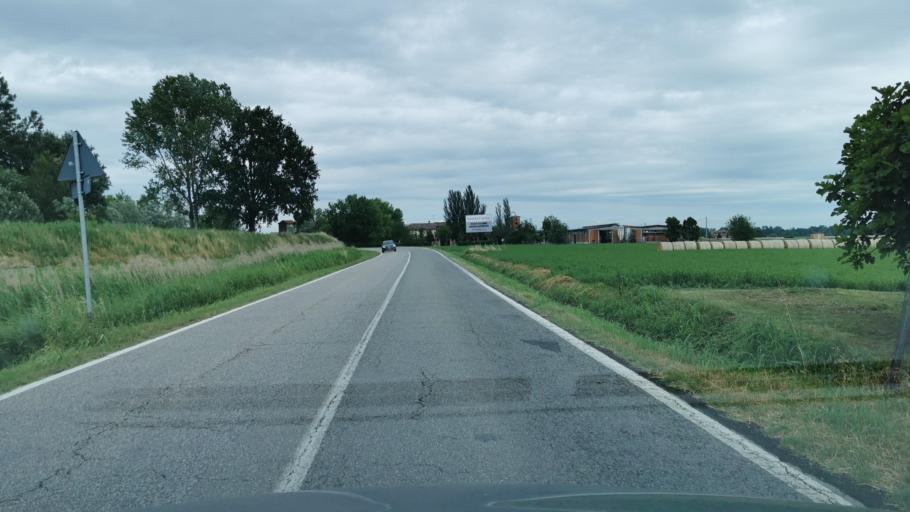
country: IT
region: Emilia-Romagna
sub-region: Provincia di Parma
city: Fidenza
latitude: 44.8949
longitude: 10.0906
